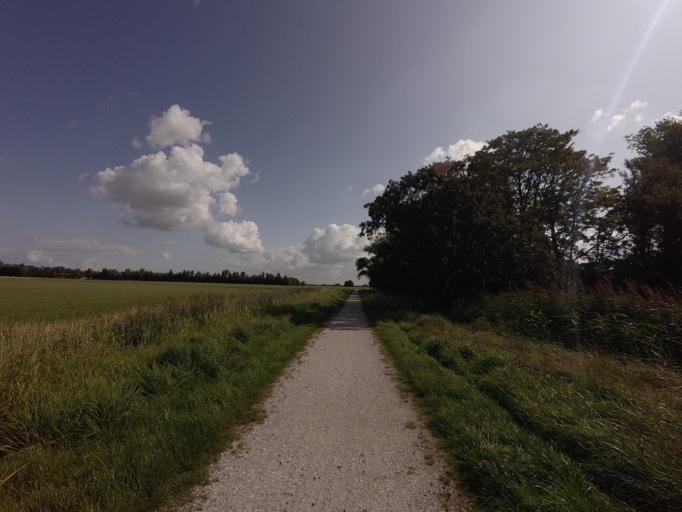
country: NL
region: Friesland
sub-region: Gemeente Het Bildt
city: Sint Annaparochie
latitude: 53.2799
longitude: 5.6675
